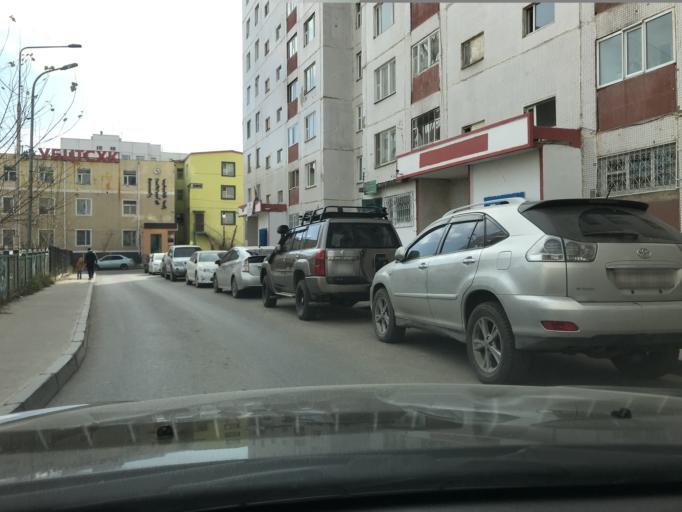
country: MN
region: Ulaanbaatar
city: Ulaanbaatar
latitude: 47.9175
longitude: 106.9363
